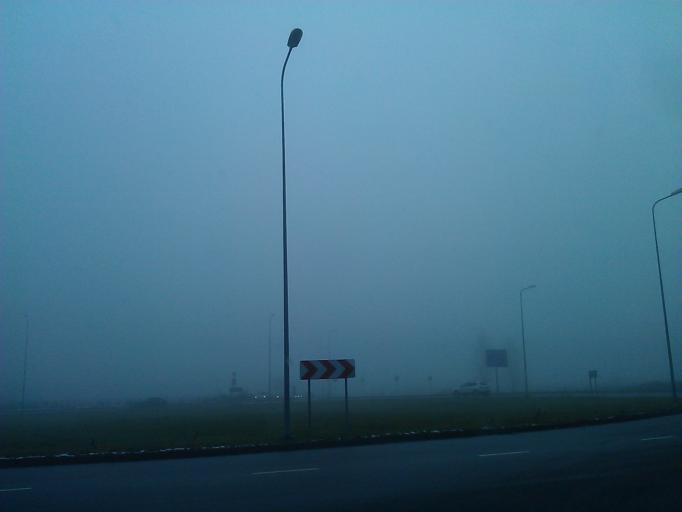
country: LV
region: Stopini
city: Ulbroka
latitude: 56.9566
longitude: 24.2524
